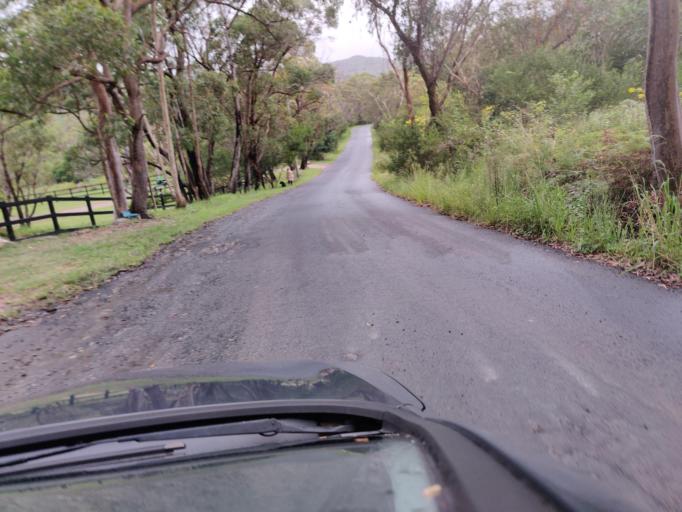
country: AU
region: New South Wales
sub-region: Pittwater
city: Ingleside
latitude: -33.6771
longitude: 151.2532
